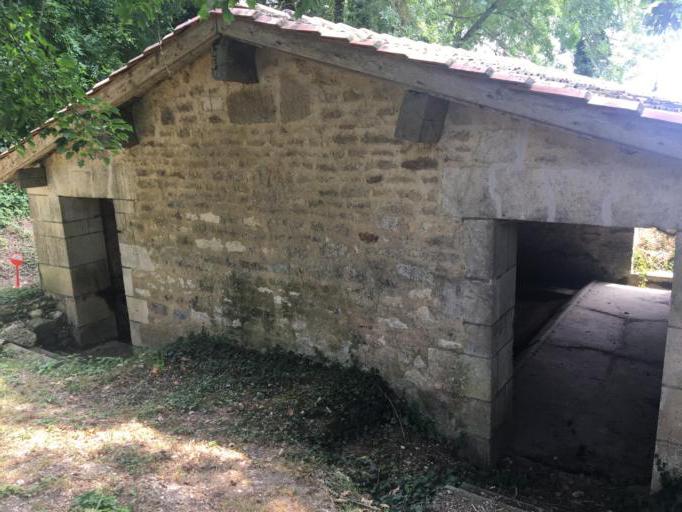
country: FR
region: Poitou-Charentes
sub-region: Departement des Deux-Sevres
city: Mauze-sur-le-Mignon
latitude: 46.0854
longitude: -0.5855
